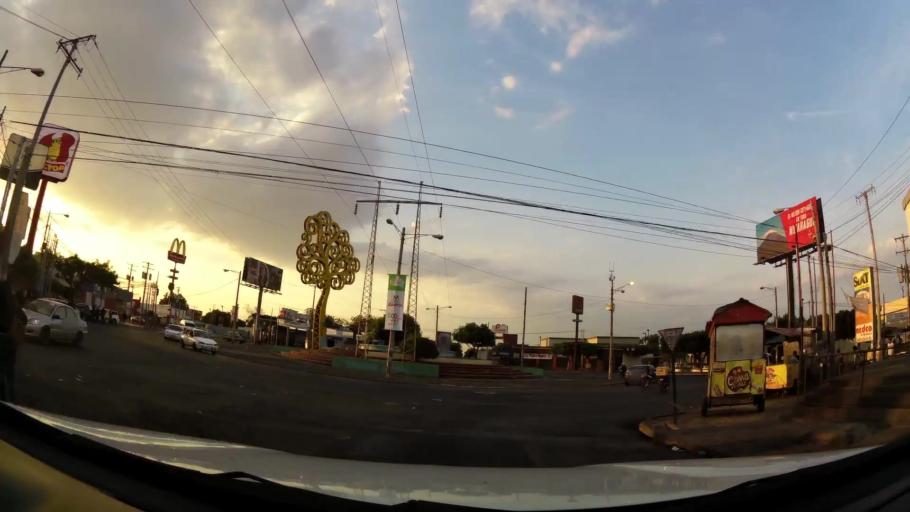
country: NI
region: Managua
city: Managua
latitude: 12.1454
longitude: -86.2339
